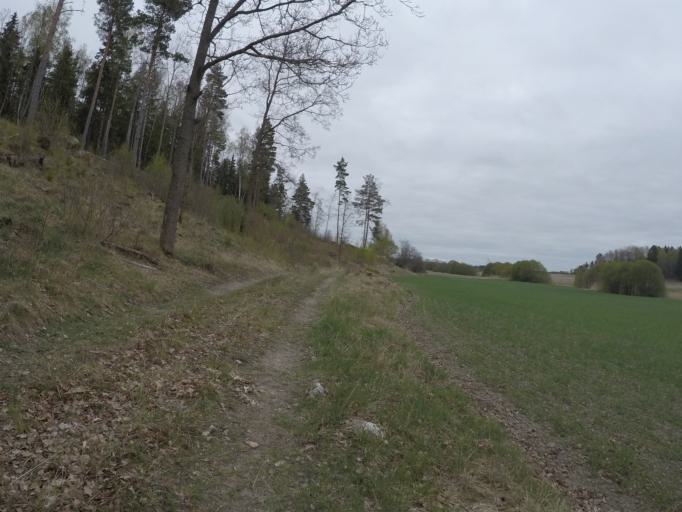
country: SE
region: Soedermanland
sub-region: Eskilstuna Kommun
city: Kvicksund
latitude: 59.4216
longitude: 16.2677
